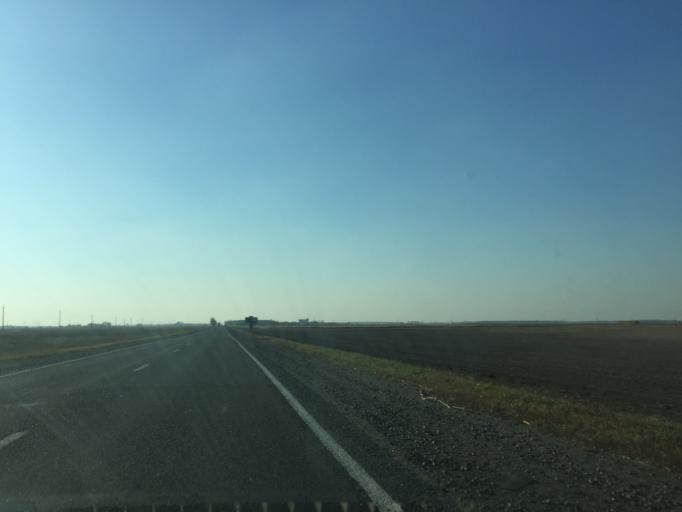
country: BY
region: Gomel
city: Dobrush
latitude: 52.3856
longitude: 31.4133
